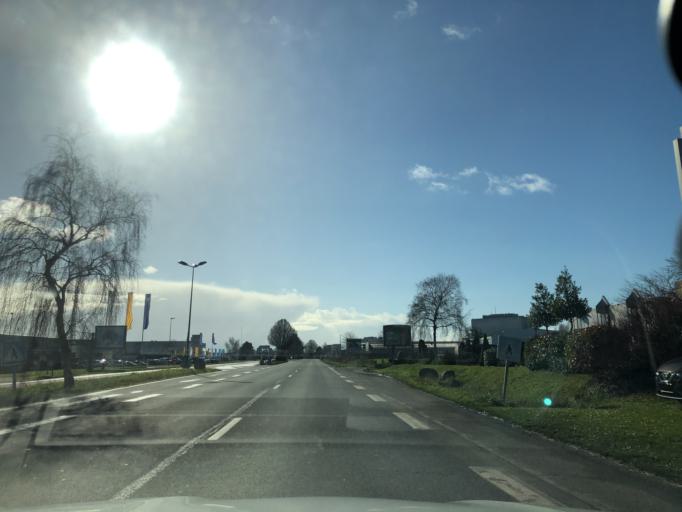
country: FR
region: Lower Normandy
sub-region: Departement du Calvados
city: Epron
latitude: 49.2113
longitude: -0.3437
